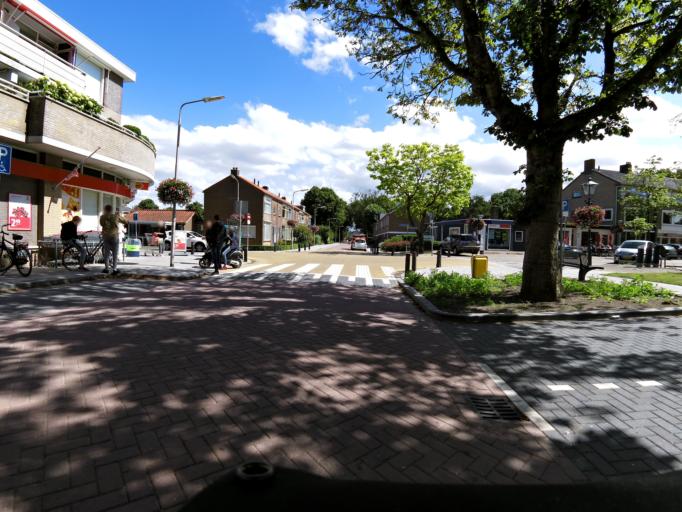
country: NL
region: South Holland
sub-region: Gemeente Zwijndrecht
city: Heerjansdam
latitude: 51.8365
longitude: 4.5642
